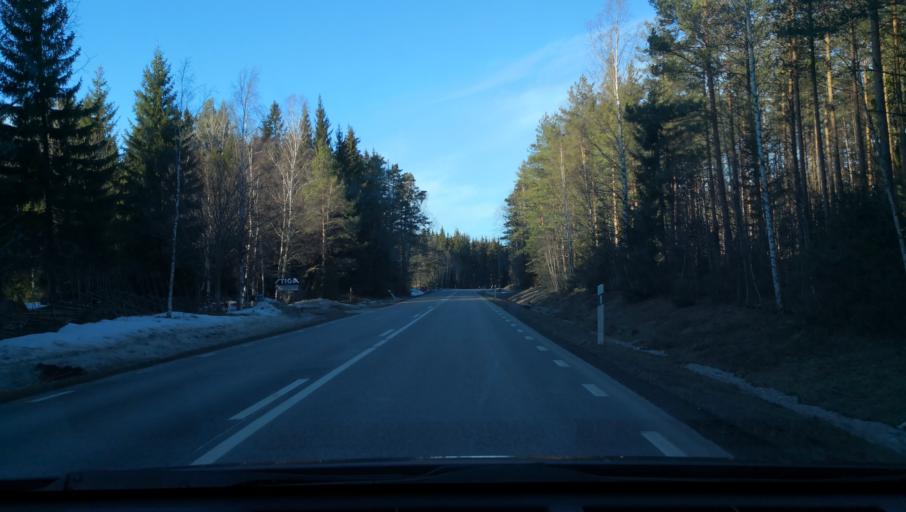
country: SE
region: Uppsala
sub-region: Osthammars Kommun
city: Gimo
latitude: 60.2090
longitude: 18.1923
